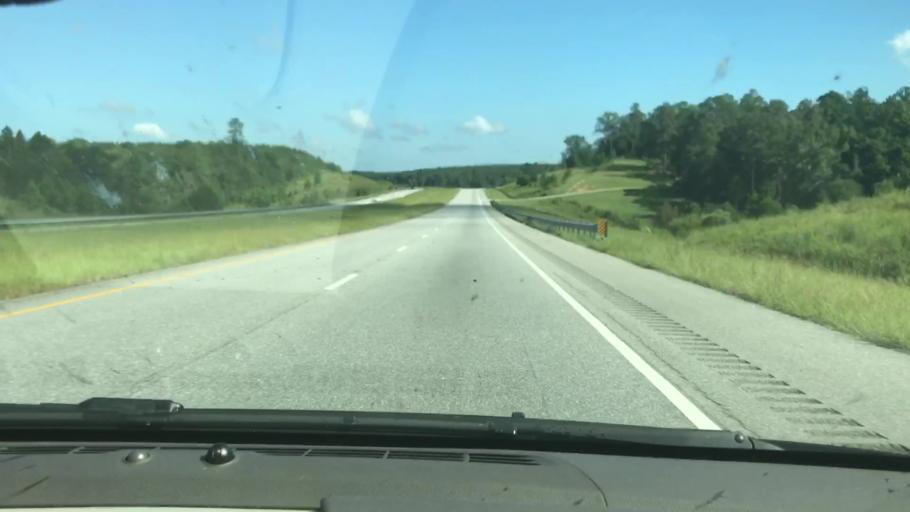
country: US
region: Alabama
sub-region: Barbour County
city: Eufaula
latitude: 32.1084
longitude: -85.1501
